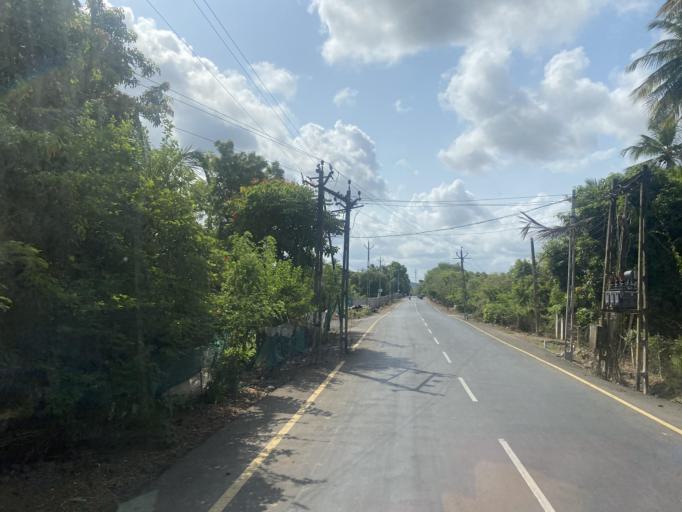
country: IN
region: Daman and Diu
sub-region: Daman District
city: Daman
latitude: 20.3301
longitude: 72.8125
